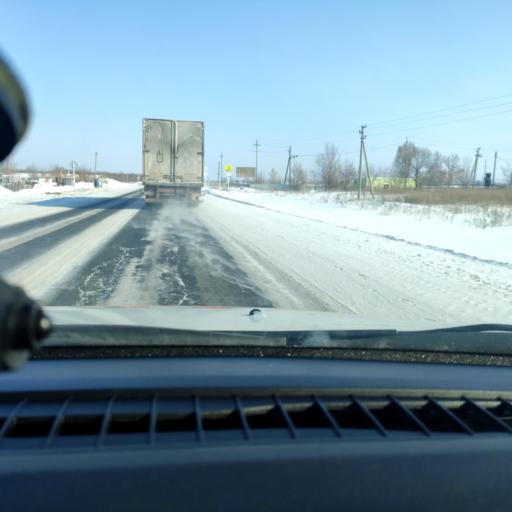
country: RU
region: Samara
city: Smyshlyayevka
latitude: 53.1835
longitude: 50.4704
